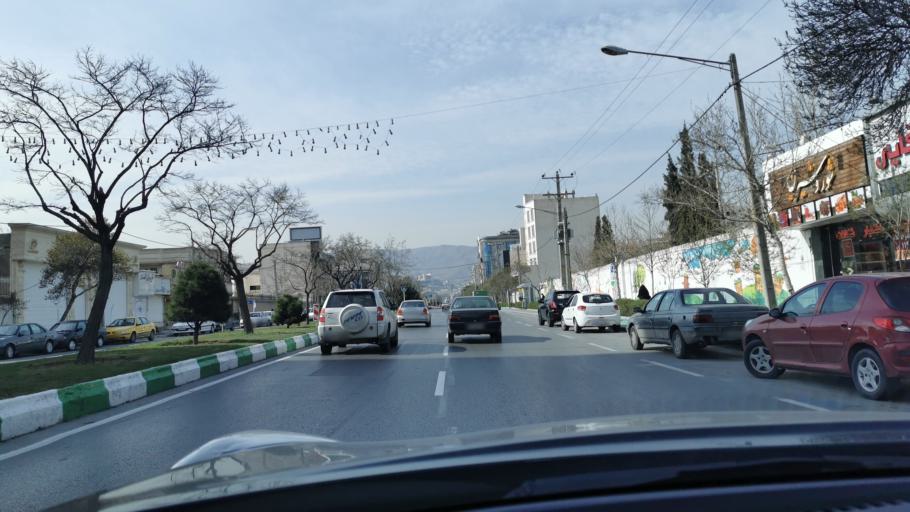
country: IR
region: Razavi Khorasan
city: Mashhad
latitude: 36.3205
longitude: 59.5132
